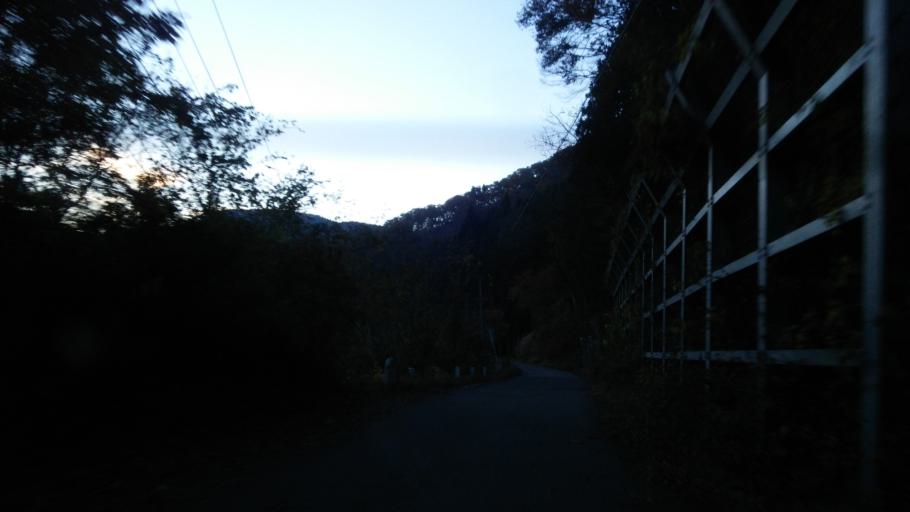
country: JP
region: Fukushima
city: Kitakata
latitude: 37.5084
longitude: 139.6910
